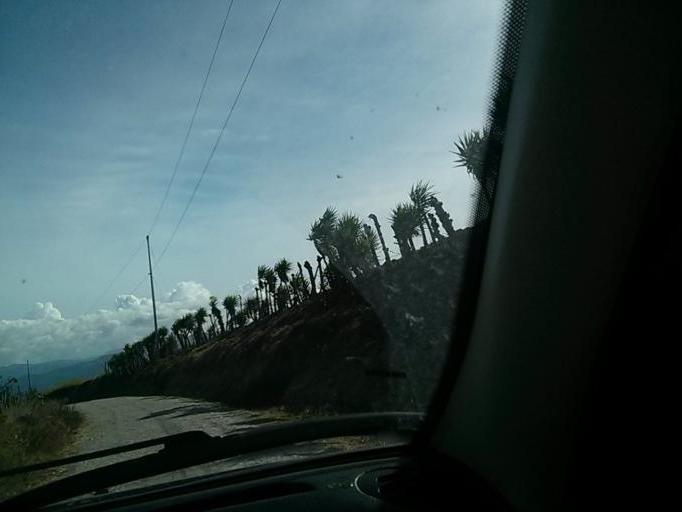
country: CR
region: Cartago
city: Cot
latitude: 9.9115
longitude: -83.9101
